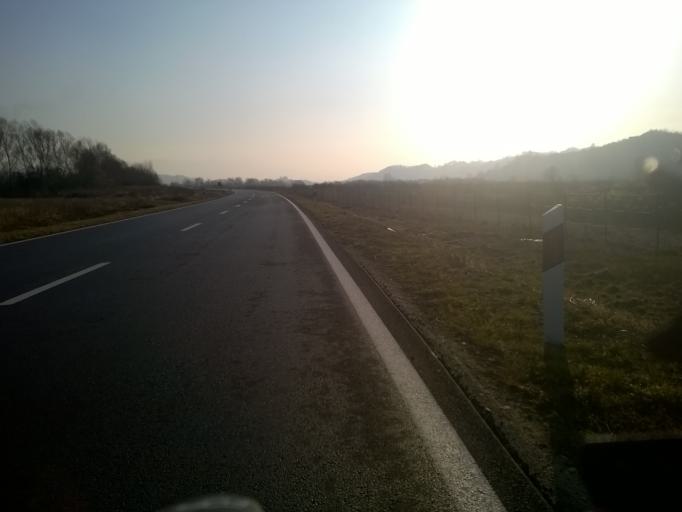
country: HR
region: Krapinsko-Zagorska
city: Zabok
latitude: 46.0667
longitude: 15.9134
